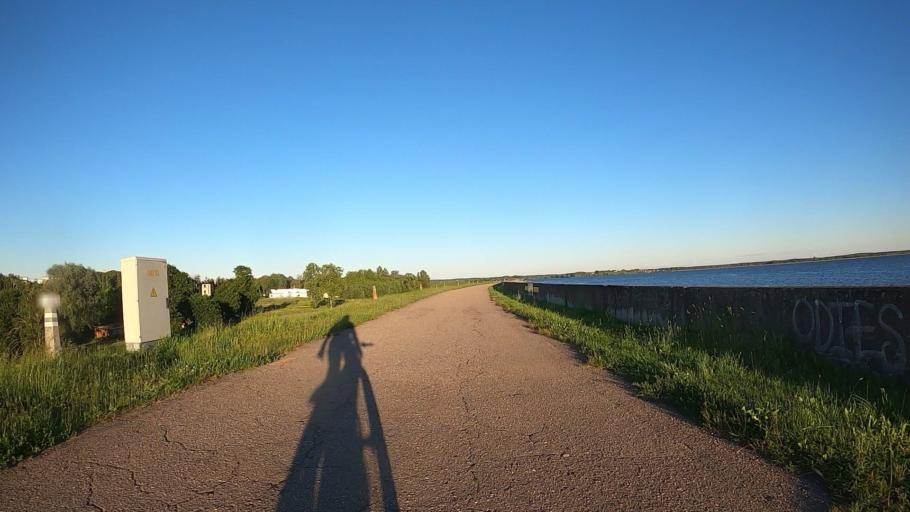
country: LV
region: Salaspils
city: Salaspils
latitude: 56.8552
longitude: 24.3179
